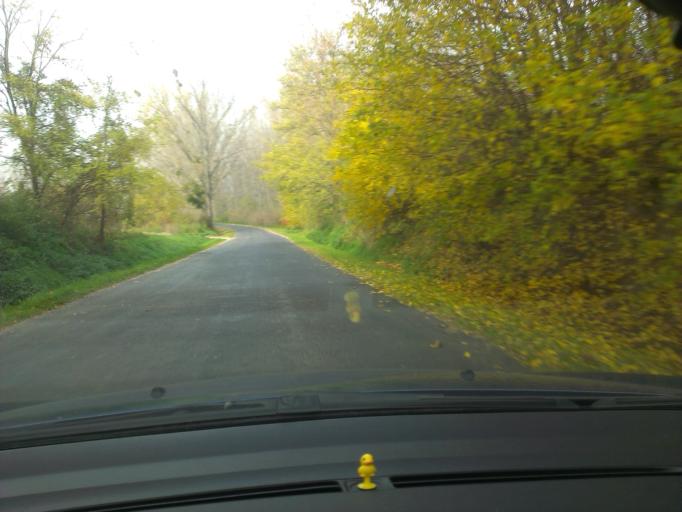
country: HU
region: Gyor-Moson-Sopron
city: Bakonyszentlaszlo
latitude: 47.3668
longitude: 17.8729
